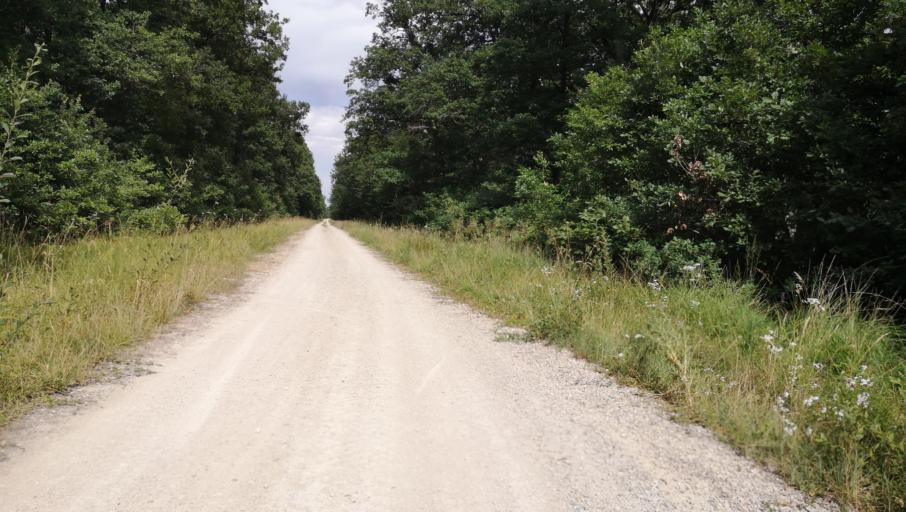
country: FR
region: Centre
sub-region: Departement du Loiret
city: Semoy
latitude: 47.9573
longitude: 1.9369
